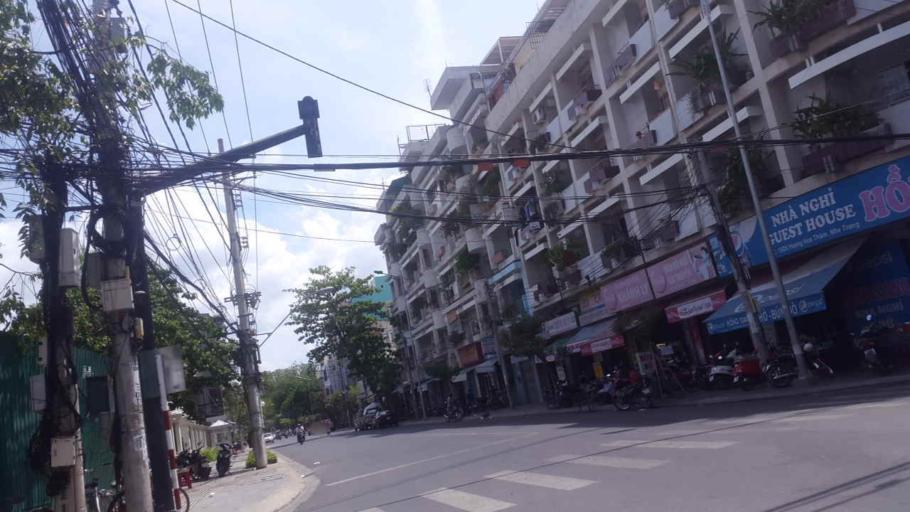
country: VN
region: Khanh Hoa
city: Nha Trang
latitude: 12.2457
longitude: 109.1939
